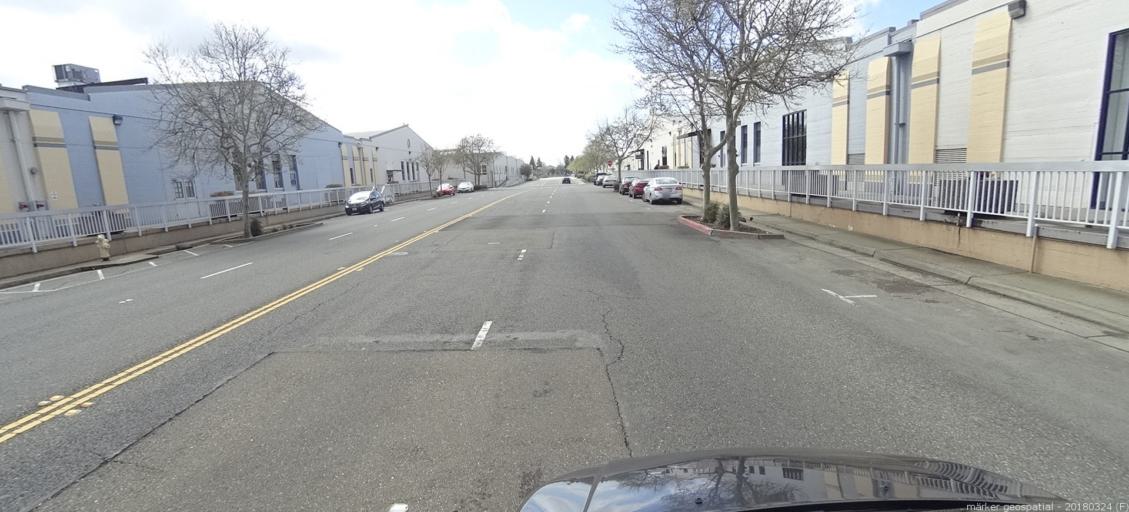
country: US
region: California
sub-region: Sacramento County
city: North Highlands
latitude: 38.6591
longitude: -121.3881
